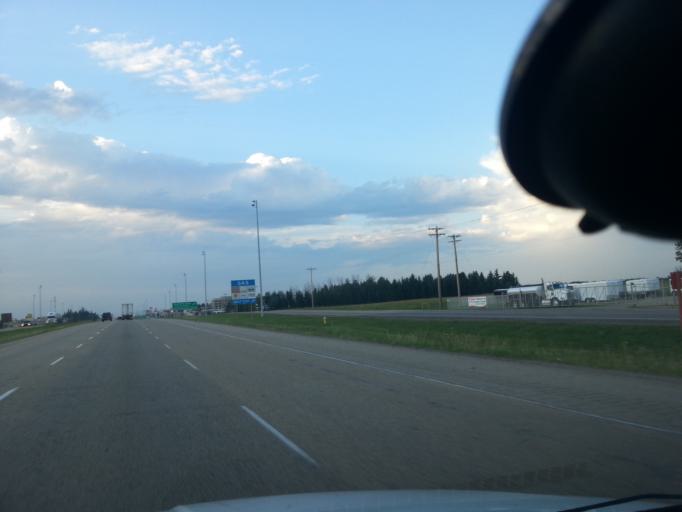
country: CA
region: Alberta
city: Red Deer
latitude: 52.2079
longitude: -113.8138
